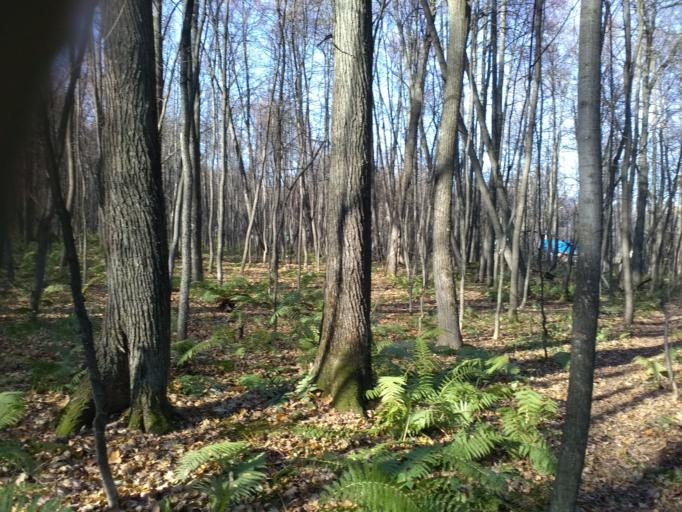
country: RU
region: Bashkortostan
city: Kudeyevskiy
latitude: 54.8046
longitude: 56.5939
